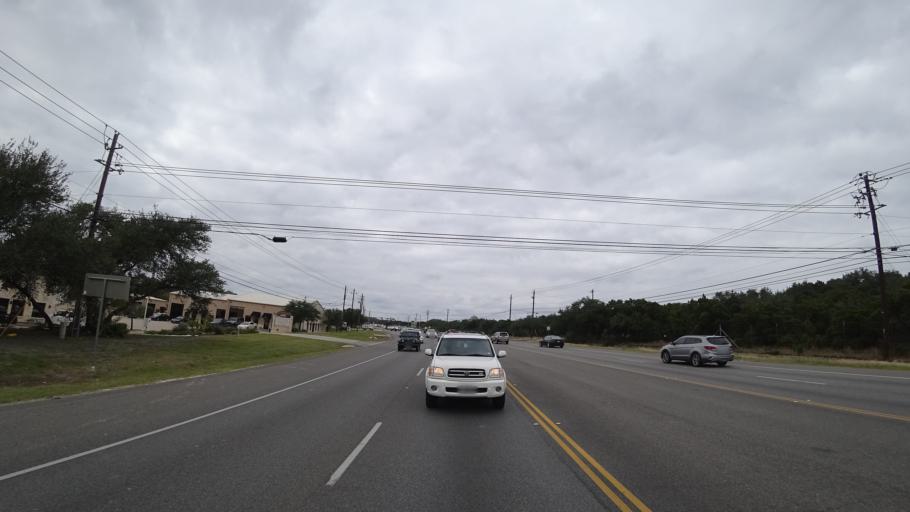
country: US
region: Texas
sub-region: Travis County
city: Bee Cave
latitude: 30.3183
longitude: -97.9507
